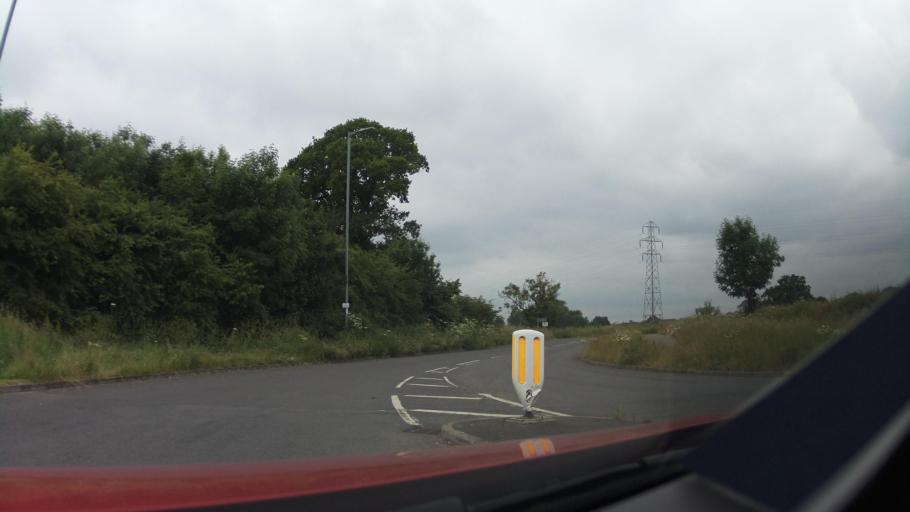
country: GB
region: England
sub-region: District of Rutland
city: Oakham
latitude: 52.6592
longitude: -0.7195
